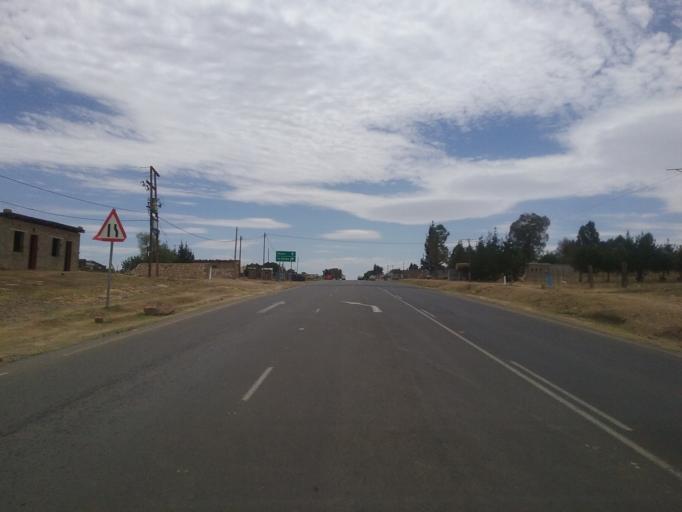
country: LS
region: Maseru
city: Maseru
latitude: -29.4913
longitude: 27.5275
